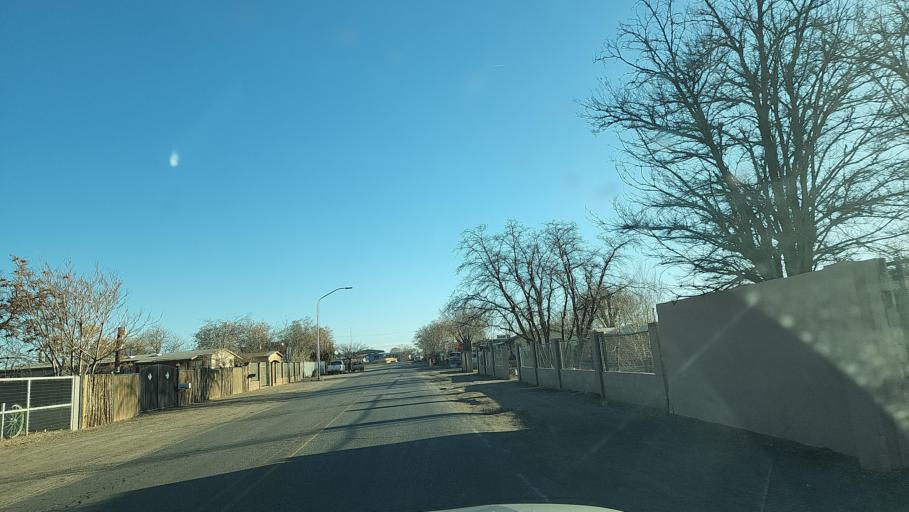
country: US
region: New Mexico
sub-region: Bernalillo County
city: South Valley
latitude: 35.0169
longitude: -106.6549
